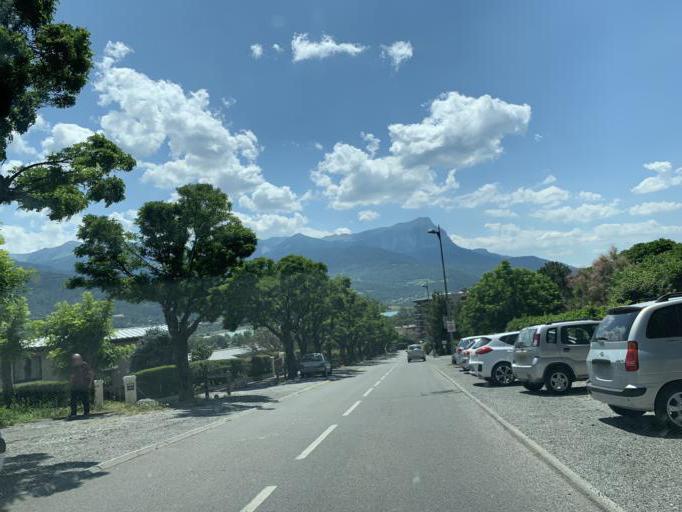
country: FR
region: Provence-Alpes-Cote d'Azur
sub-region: Departement des Hautes-Alpes
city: Embrun
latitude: 44.5548
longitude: 6.4806
